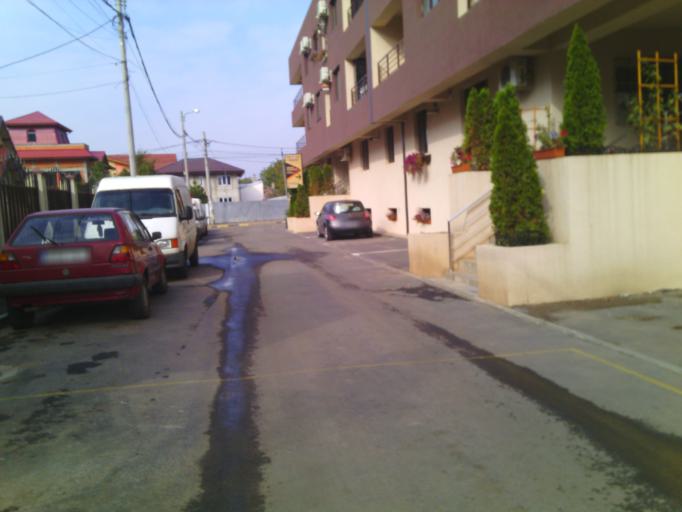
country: RO
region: Ilfov
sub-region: Comuna Magurele
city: Magurele
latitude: 44.3886
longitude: 26.0602
